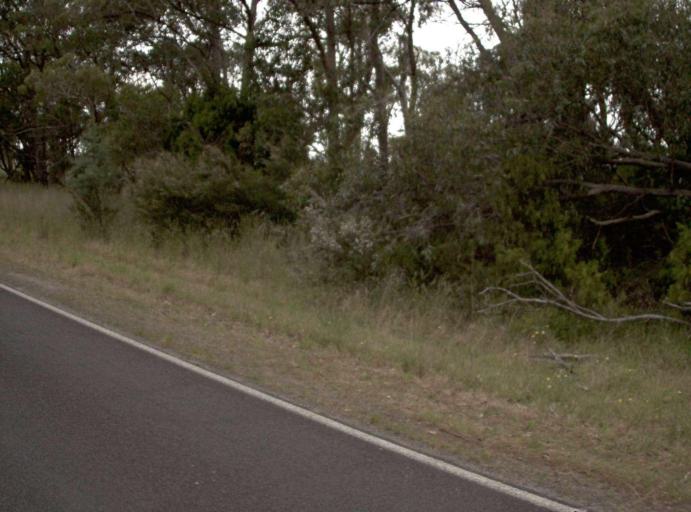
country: AU
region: Victoria
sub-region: Latrobe
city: Traralgon
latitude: -38.5343
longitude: 146.8542
